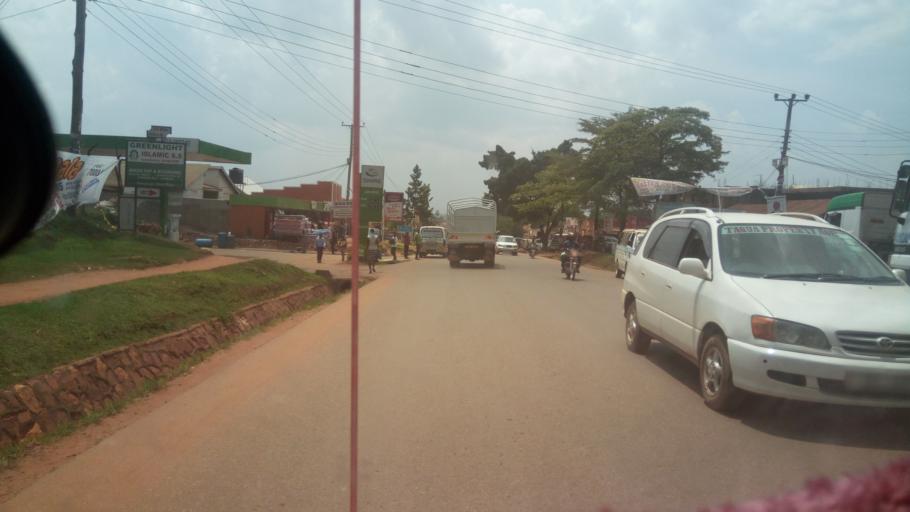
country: UG
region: Central Region
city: Kampala Central Division
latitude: 0.3693
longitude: 32.5227
